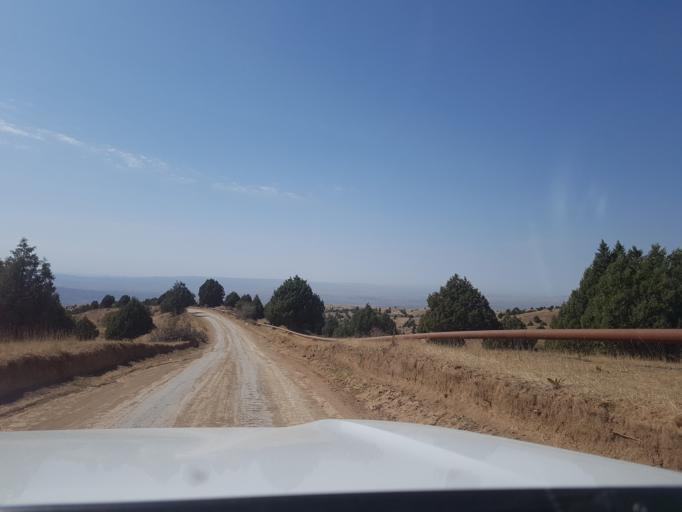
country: TM
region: Ahal
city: Baharly
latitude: 38.3164
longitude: 56.9536
